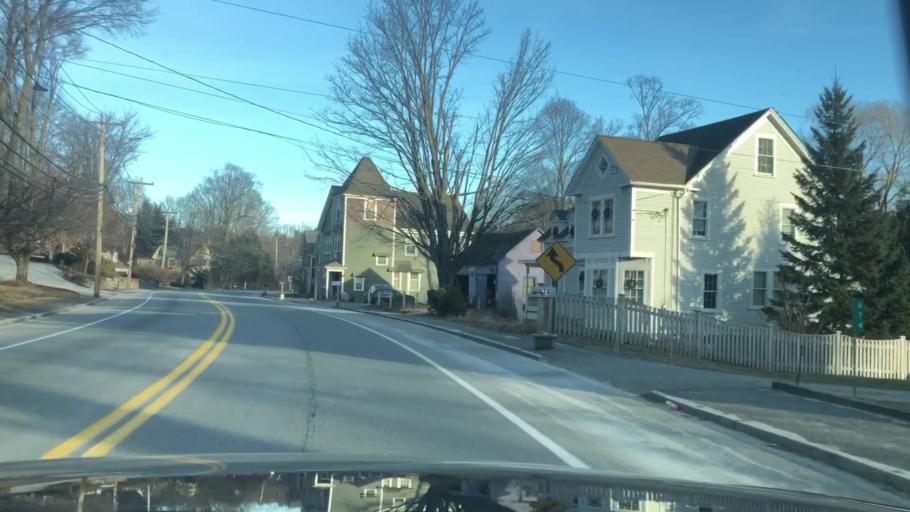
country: US
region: Massachusetts
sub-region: Worcester County
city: Bolton
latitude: 42.4329
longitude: -71.6062
